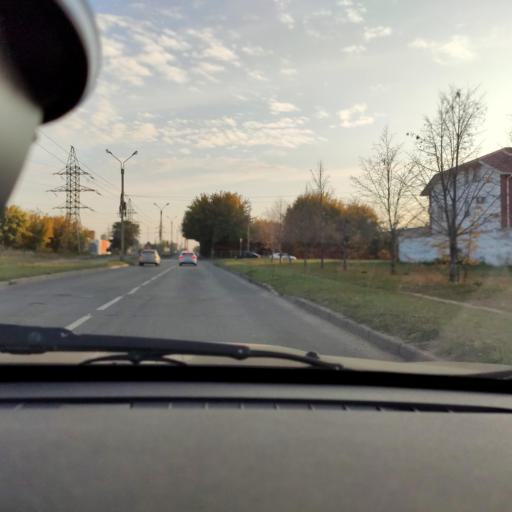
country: RU
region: Samara
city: Tol'yatti
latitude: 53.5555
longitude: 49.3189
